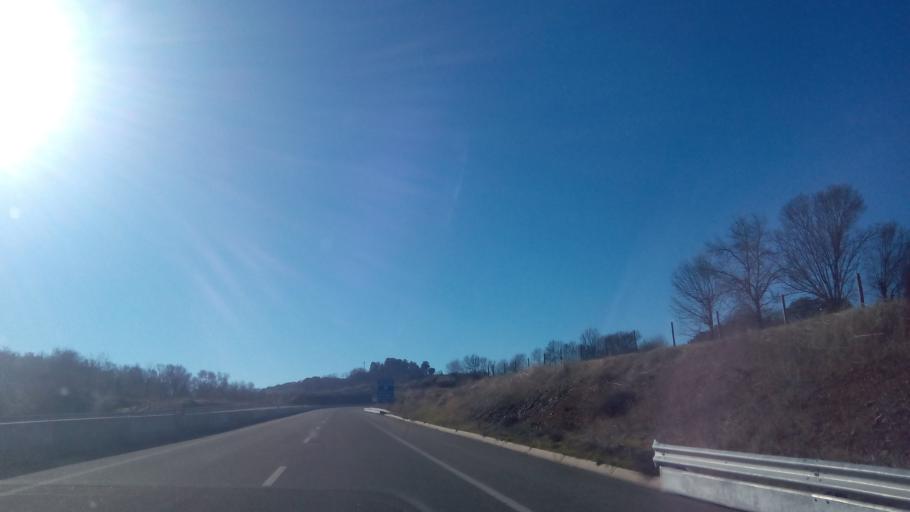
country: PT
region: Braganca
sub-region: Braganca Municipality
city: Braganca
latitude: 41.7777
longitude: -6.7473
